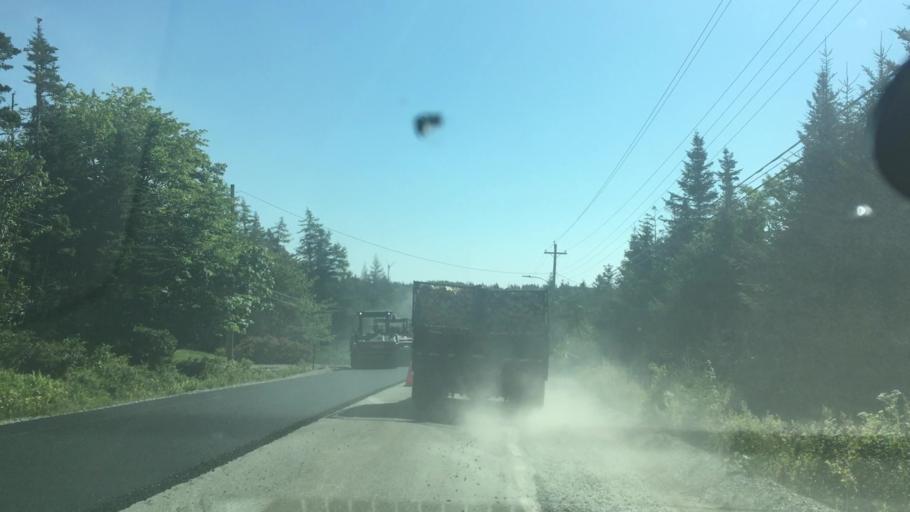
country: CA
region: Nova Scotia
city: New Glasgow
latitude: 44.9081
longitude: -62.4985
